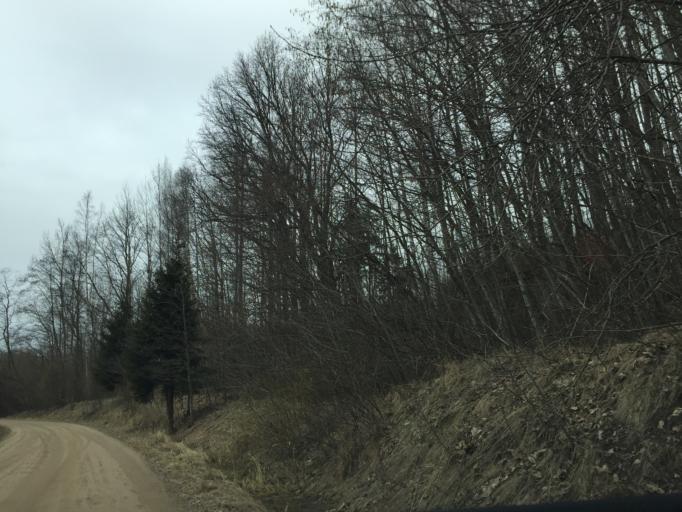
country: LV
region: Kraslavas Rajons
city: Kraslava
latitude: 55.9809
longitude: 27.1597
